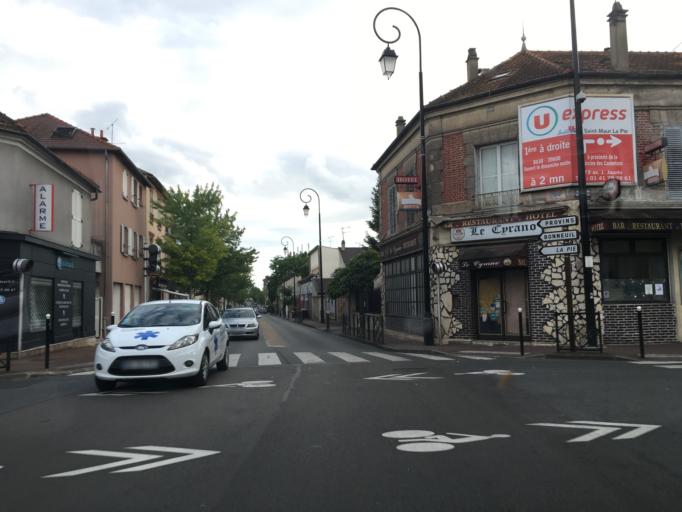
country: FR
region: Ile-de-France
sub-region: Departement du Val-de-Marne
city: Saint-Maur-des-Fosses
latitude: 48.7892
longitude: 2.4953
